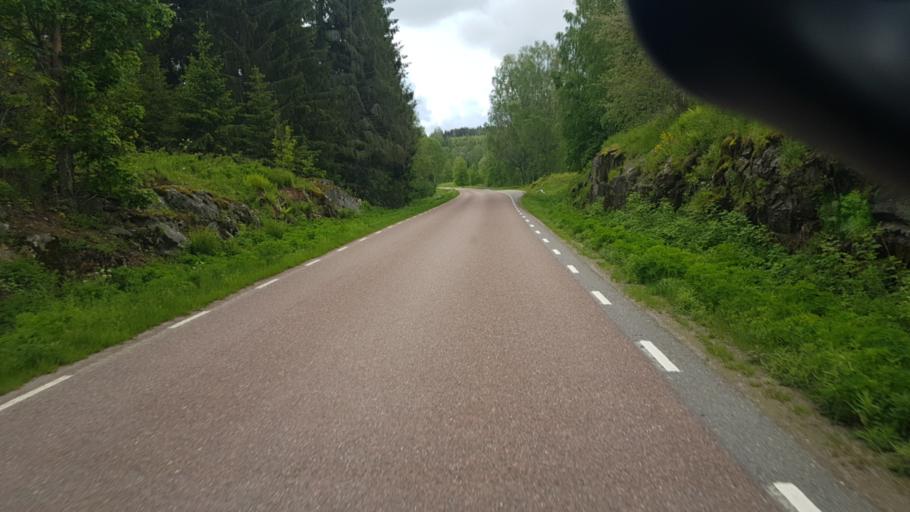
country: NO
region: Hedmark
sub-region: Eidskog
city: Skotterud
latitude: 59.7549
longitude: 12.0537
